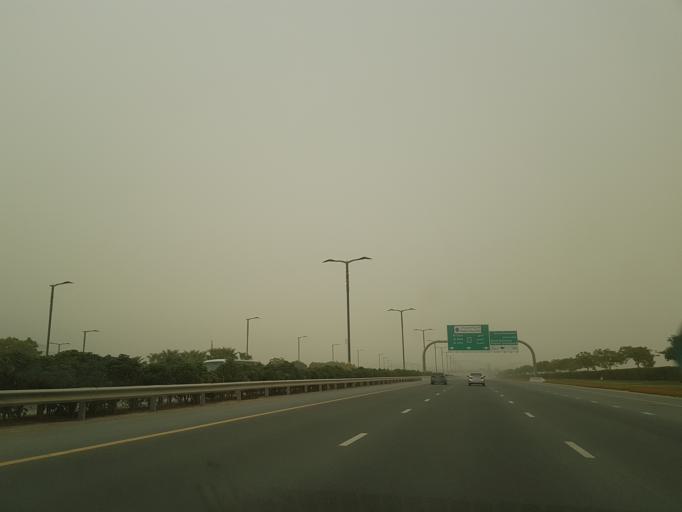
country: AE
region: Dubai
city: Dubai
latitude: 25.1656
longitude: 55.3011
